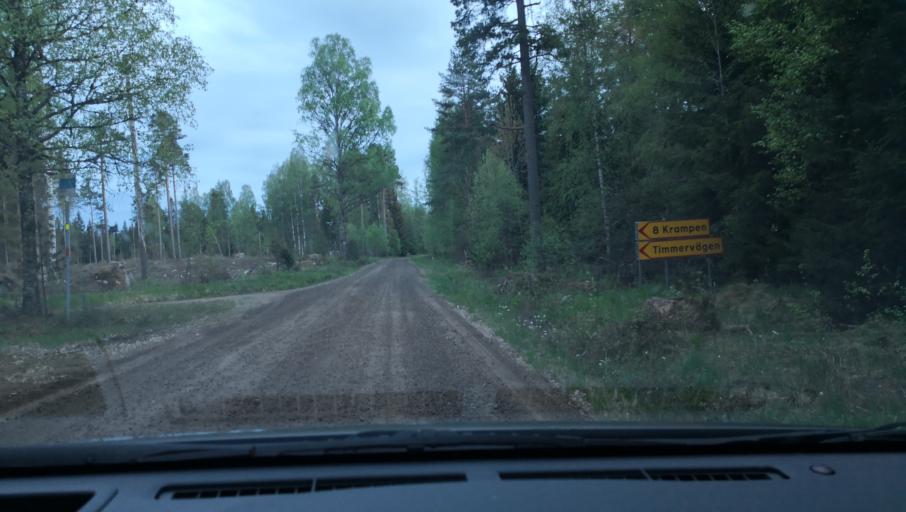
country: SE
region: Vaestmanland
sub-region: Skinnskattebergs Kommun
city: Skinnskatteberg
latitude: 59.7037
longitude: 15.5153
